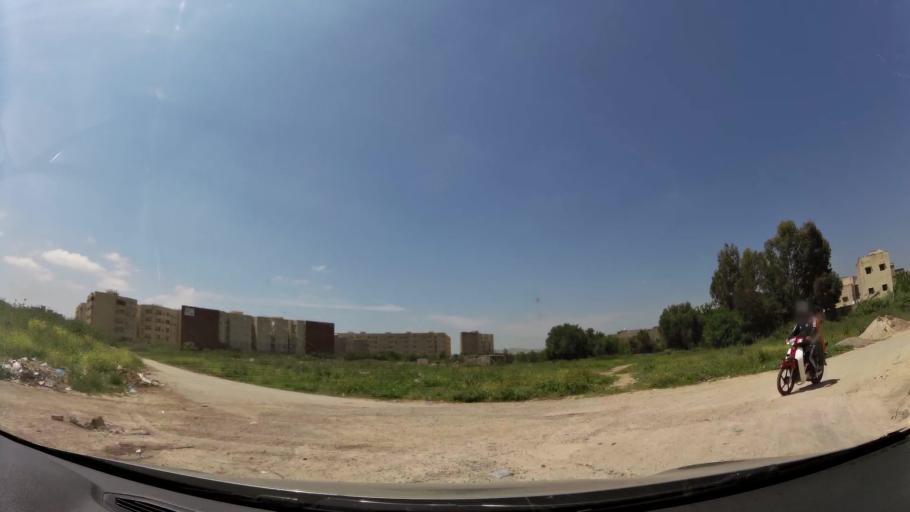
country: MA
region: Fes-Boulemane
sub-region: Fes
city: Fes
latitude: 34.0254
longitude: -5.0472
